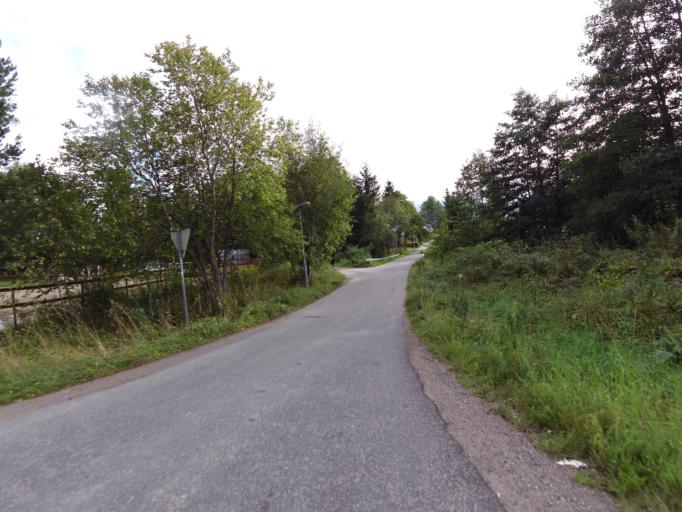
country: SE
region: Gaevleborg
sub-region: Gavle Kommun
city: Gavle
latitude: 60.6650
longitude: 17.1928
